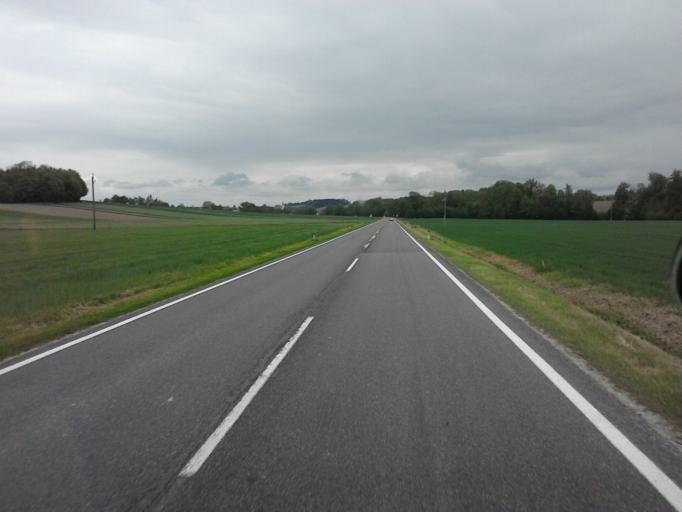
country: AT
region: Upper Austria
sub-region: Politischer Bezirk Vocklabruck
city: Wolfsegg am Hausruck
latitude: 48.2018
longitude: 13.6553
